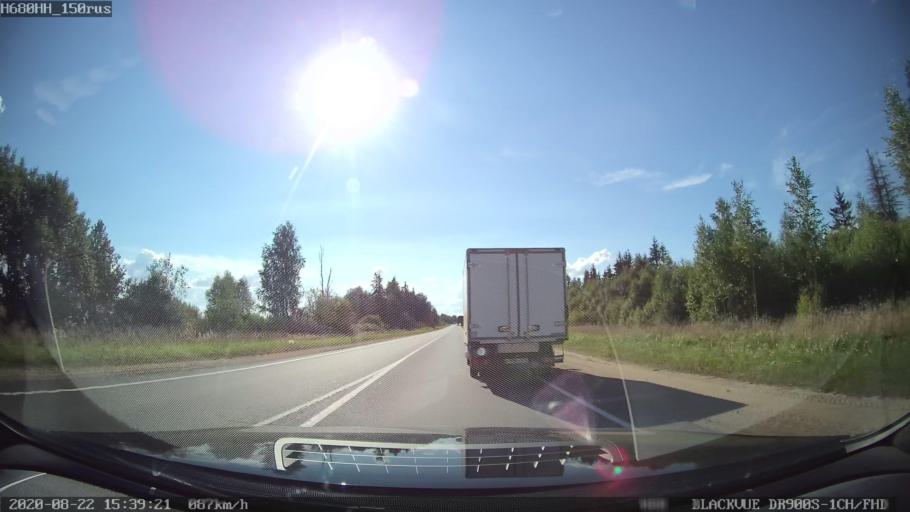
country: RU
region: Tverskaya
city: Bezhetsk
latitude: 57.7577
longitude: 36.6269
